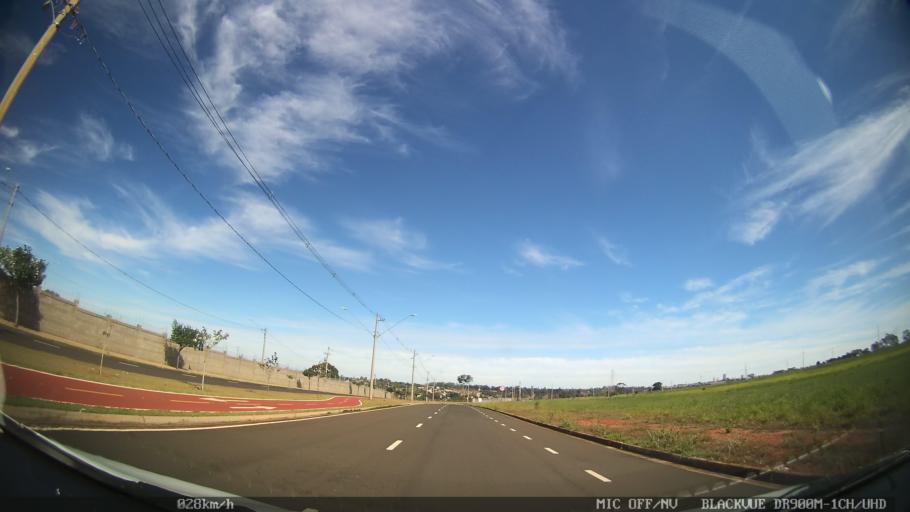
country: BR
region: Sao Paulo
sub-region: Sao Jose Do Rio Preto
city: Sao Jose do Rio Preto
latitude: -20.8524
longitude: -49.3744
